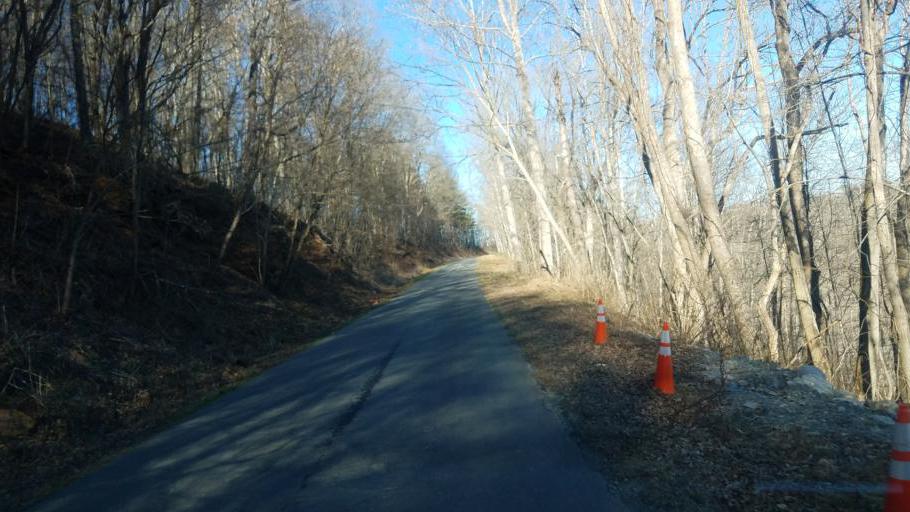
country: US
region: Virginia
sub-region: Pulaski County
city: Pulaski
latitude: 37.1671
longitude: -80.8599
